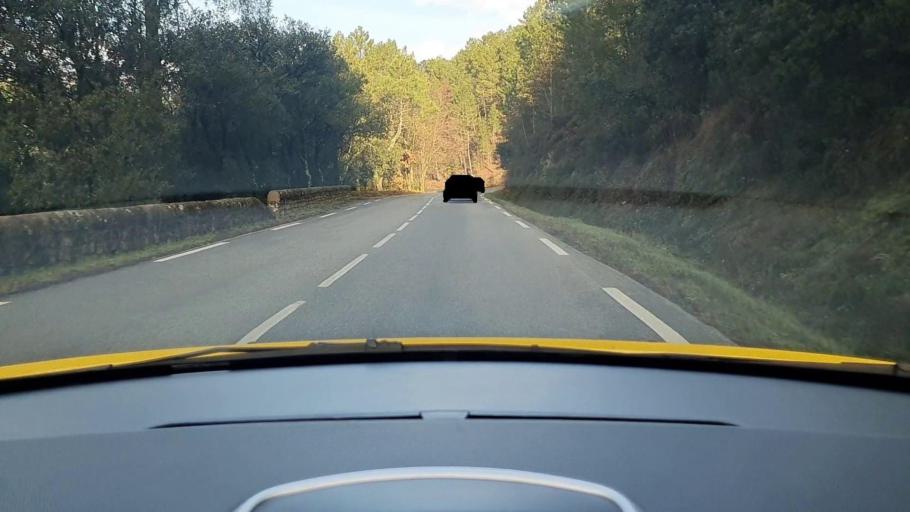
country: FR
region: Languedoc-Roussillon
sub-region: Departement du Gard
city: Branoux-les-Taillades
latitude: 44.3147
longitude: 3.9689
